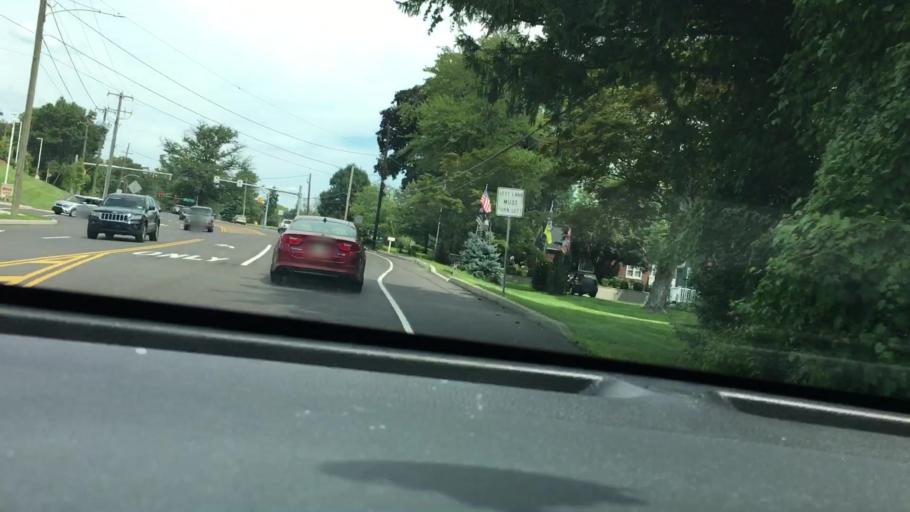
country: US
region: Pennsylvania
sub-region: Bucks County
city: Trevose
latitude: 40.1383
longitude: -74.9896
